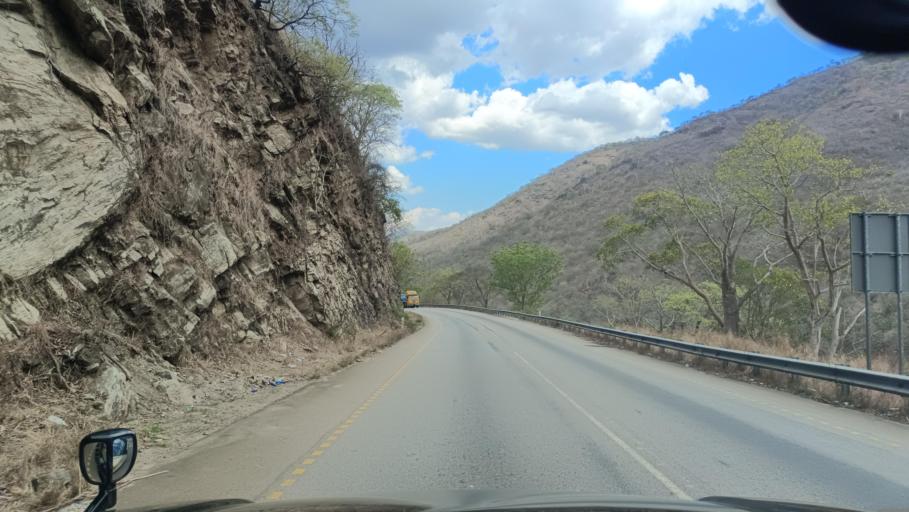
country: TZ
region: Morogoro
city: Kidatu
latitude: -7.5743
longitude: 36.7419
